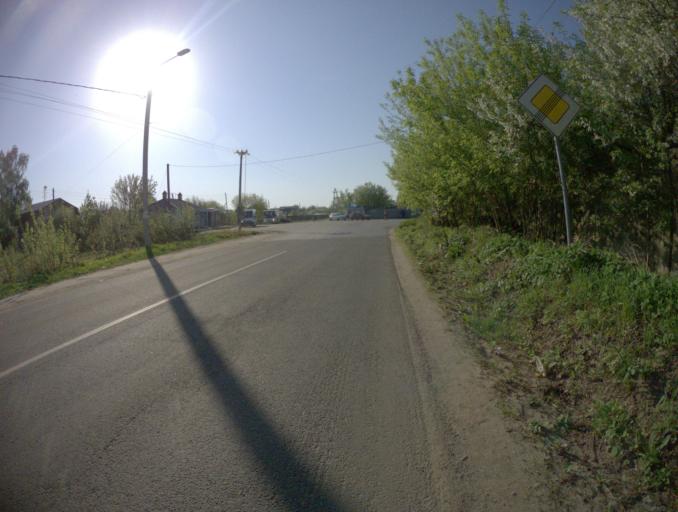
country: RU
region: Vladimir
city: Novovyazniki
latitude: 56.2029
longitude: 42.1689
